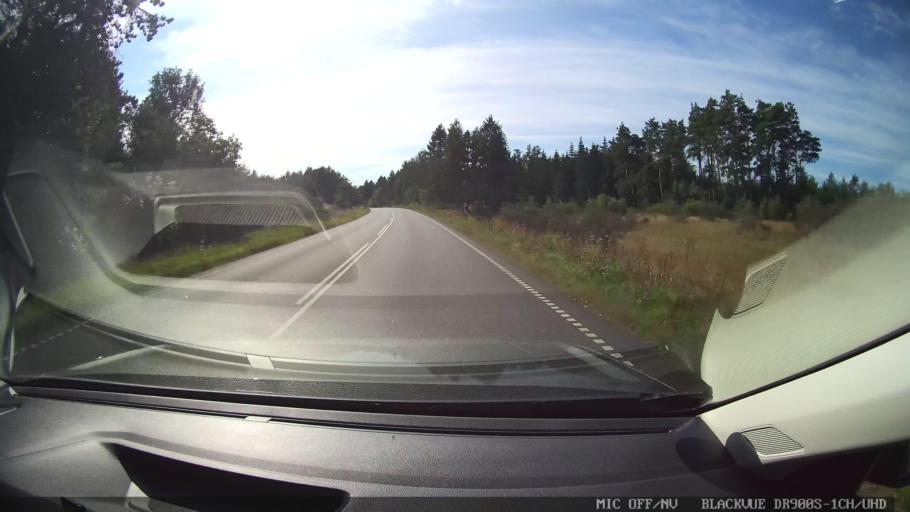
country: DK
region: North Denmark
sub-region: Mariagerfjord Kommune
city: Hadsund
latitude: 56.7348
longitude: 10.0791
